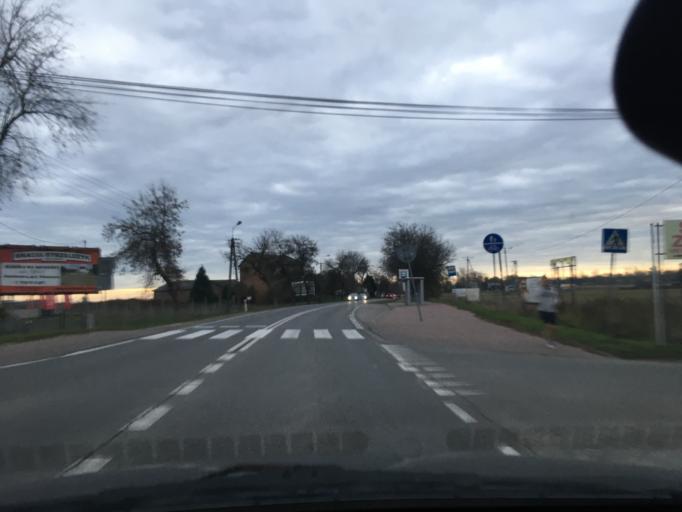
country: PL
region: Masovian Voivodeship
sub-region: Powiat piaseczynski
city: Lesznowola
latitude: 52.0958
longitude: 20.9238
